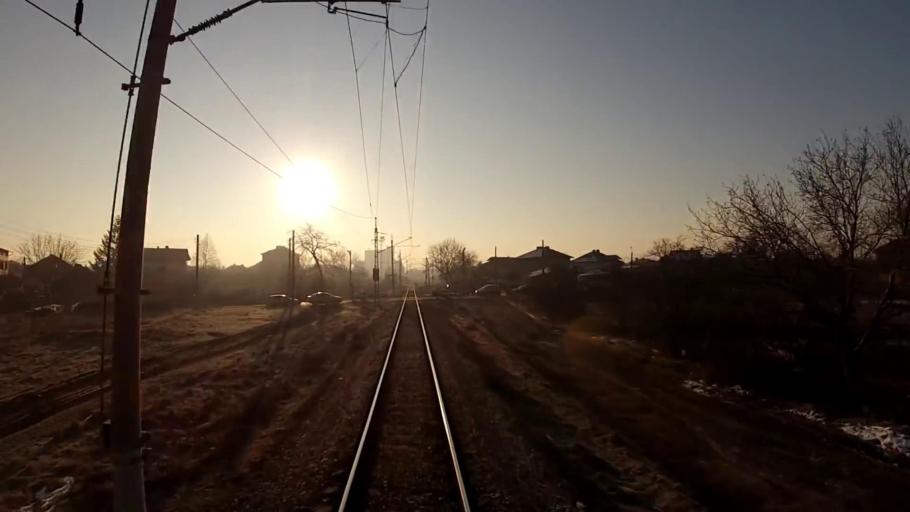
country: BG
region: Sofiya
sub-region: Obshtina Kostinbrod
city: Kostinbrod
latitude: 42.8029
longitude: 23.2027
